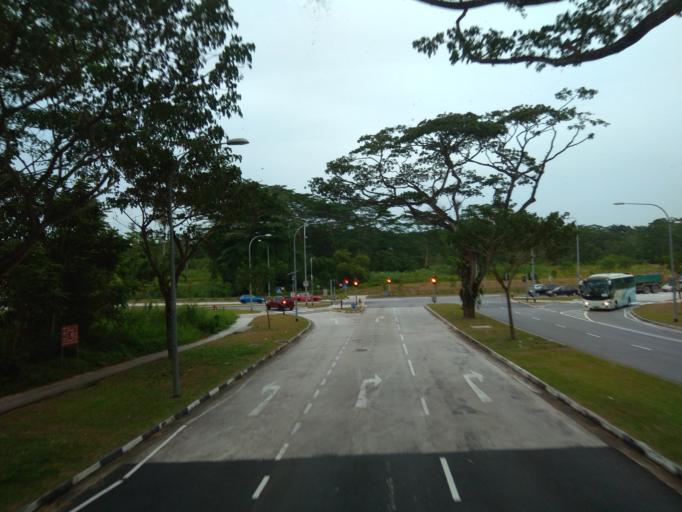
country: MY
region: Johor
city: Johor Bahru
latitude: 1.3571
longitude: 103.6944
